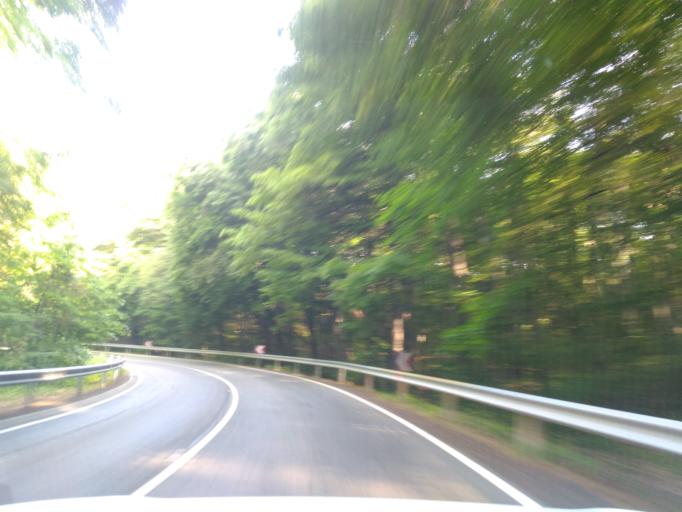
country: HU
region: Baranya
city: Komlo
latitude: 46.1794
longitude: 18.2649
